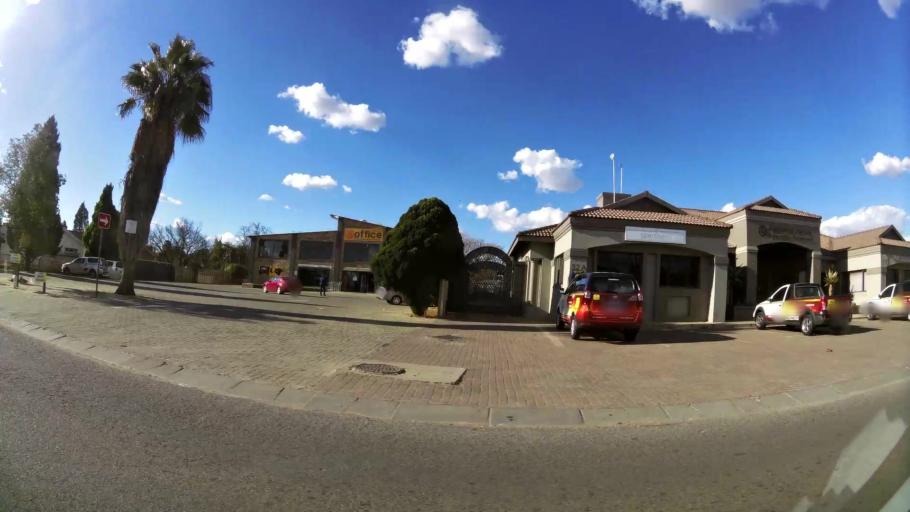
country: ZA
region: North-West
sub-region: Dr Kenneth Kaunda District Municipality
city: Klerksdorp
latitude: -26.8499
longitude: 26.6762
